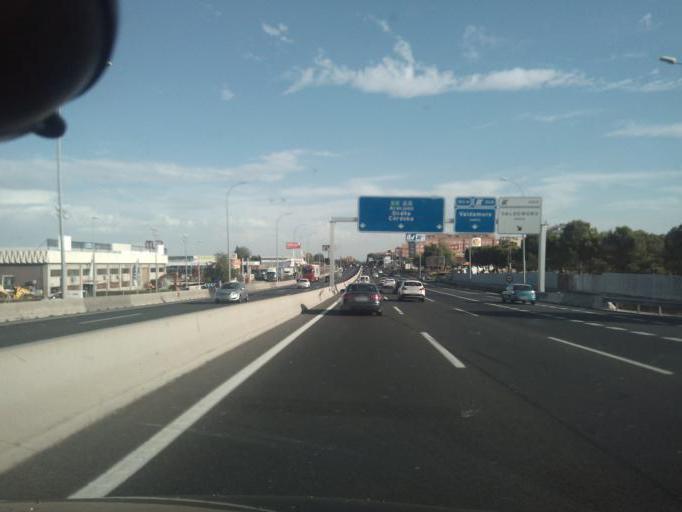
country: ES
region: Madrid
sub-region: Provincia de Madrid
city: Valdemoro
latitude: 40.2007
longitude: -3.6778
